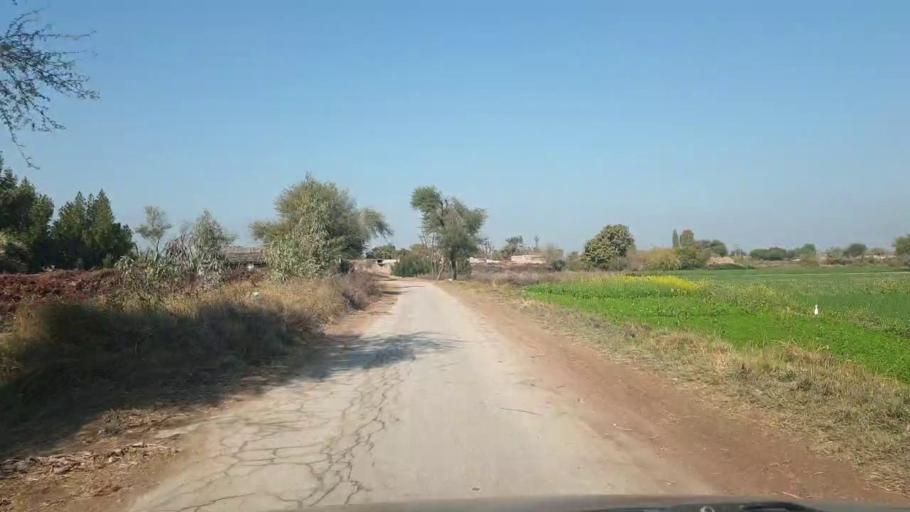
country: PK
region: Sindh
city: Shahdadpur
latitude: 25.8867
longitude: 68.5416
